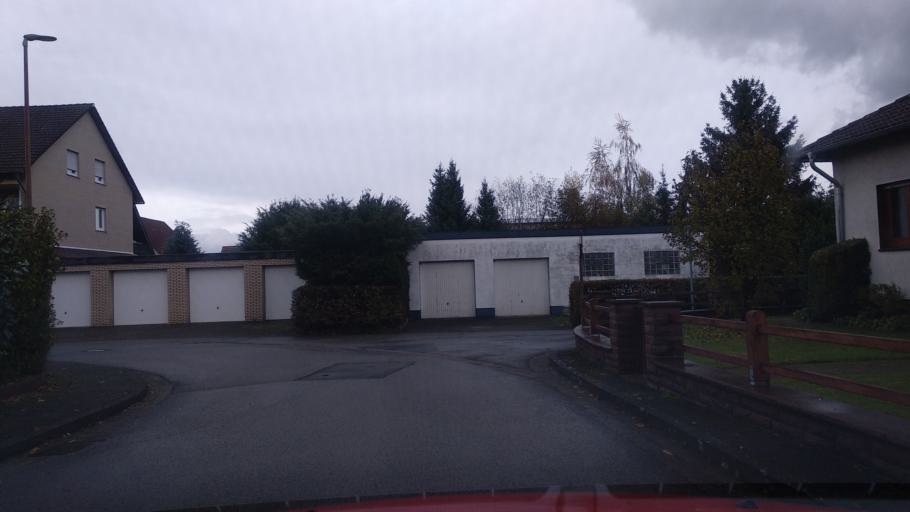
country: DE
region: North Rhine-Westphalia
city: Beverungen
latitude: 51.6686
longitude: 9.3798
